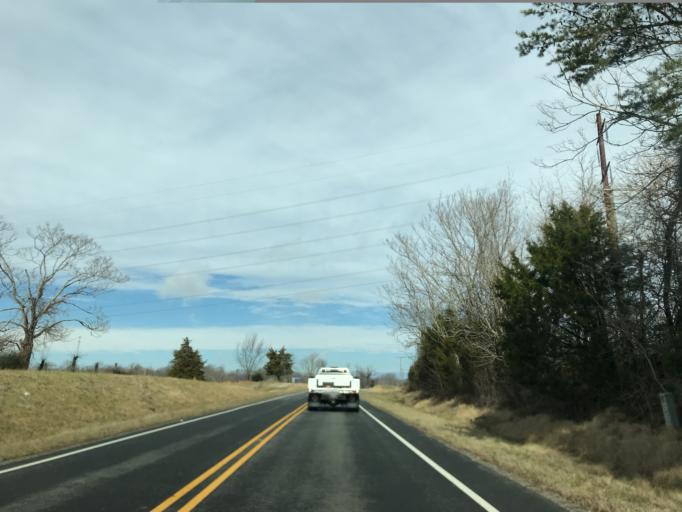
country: US
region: Virginia
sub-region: King George County
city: Dahlgren
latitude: 38.3250
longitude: -77.0815
